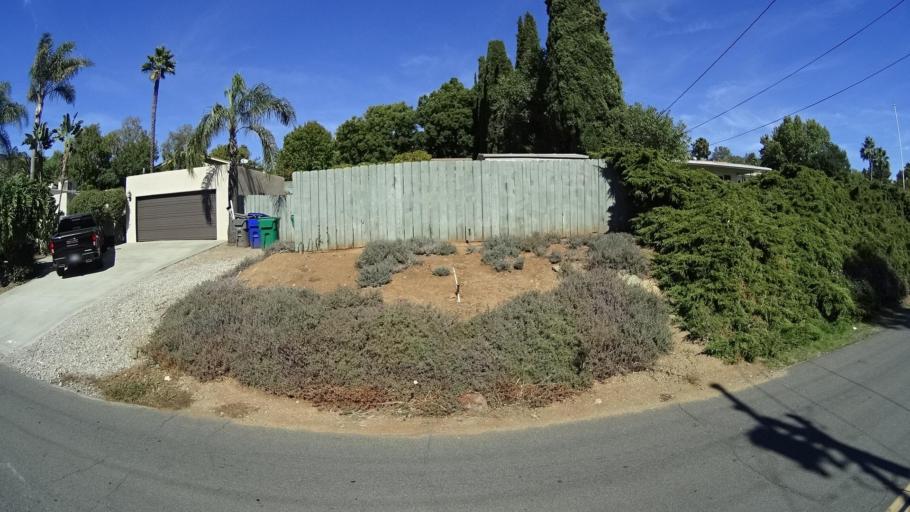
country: US
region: California
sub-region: San Diego County
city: Casa de Oro-Mount Helix
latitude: 32.7555
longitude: -116.9675
